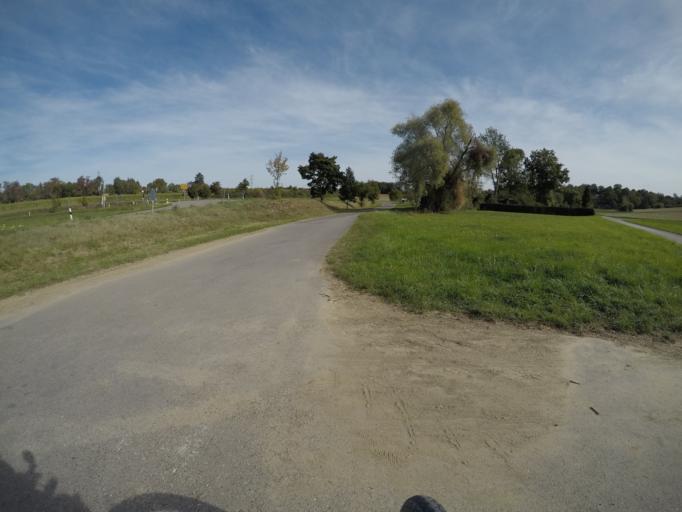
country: DE
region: Baden-Wuerttemberg
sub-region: Regierungsbezirk Stuttgart
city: Schwieberdingen
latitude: 48.8610
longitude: 9.0944
